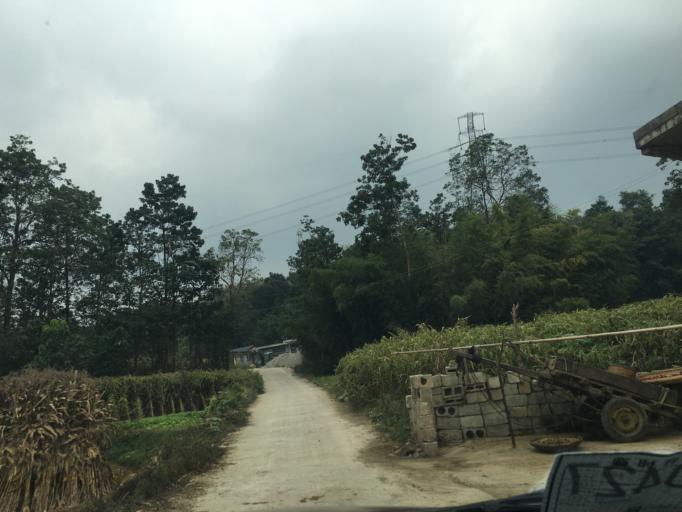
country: CN
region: Guangxi Zhuangzu Zizhiqu
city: Xinzhou
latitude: 25.5655
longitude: 105.6077
